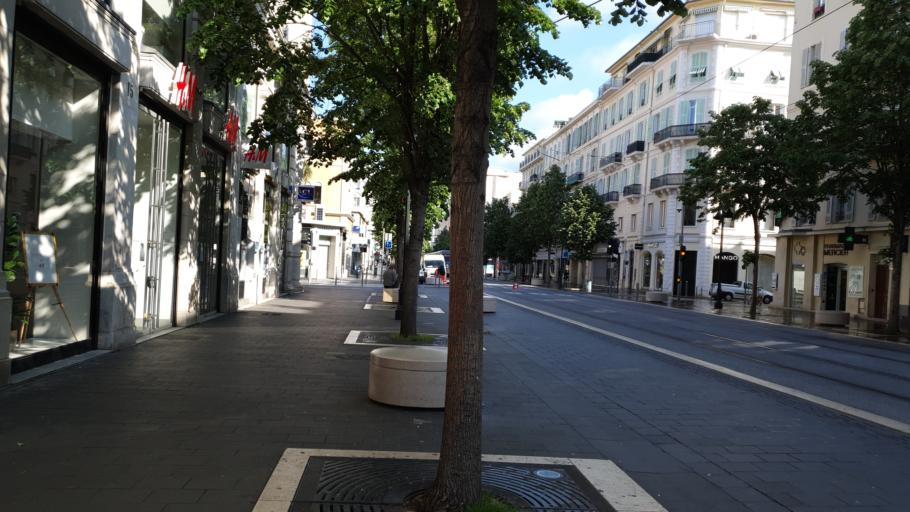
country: FR
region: Provence-Alpes-Cote d'Azur
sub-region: Departement des Alpes-Maritimes
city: Nice
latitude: 43.6995
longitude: 7.2687
